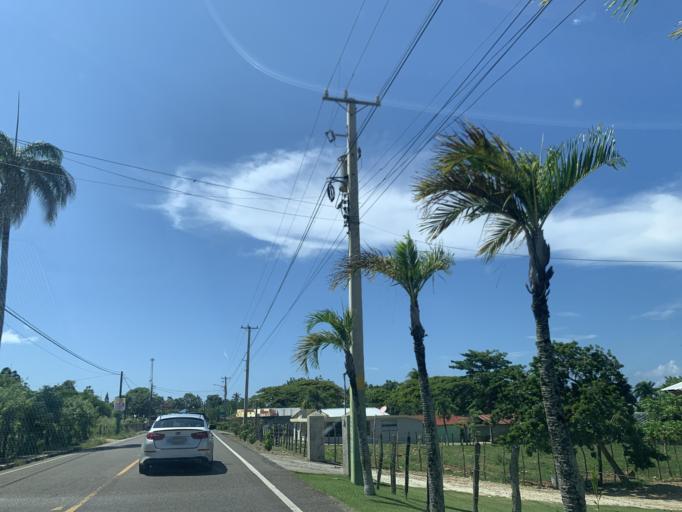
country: DO
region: Maria Trinidad Sanchez
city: Cabrera
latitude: 19.6697
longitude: -69.9531
